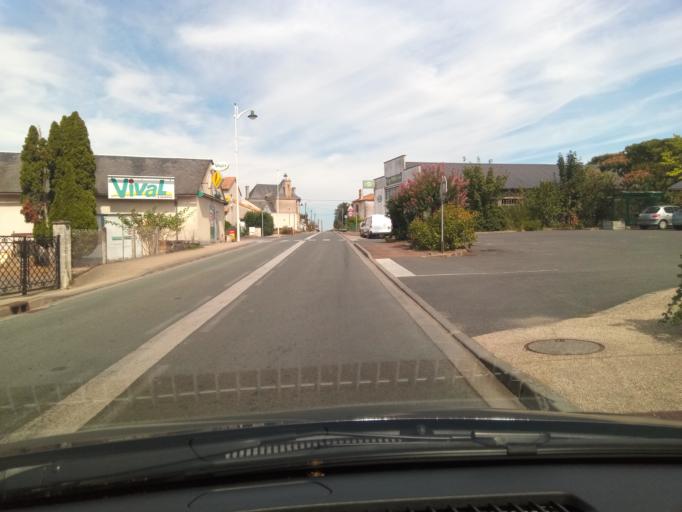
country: FR
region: Poitou-Charentes
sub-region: Departement de la Vienne
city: Terce
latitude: 46.5169
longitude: 0.5638
